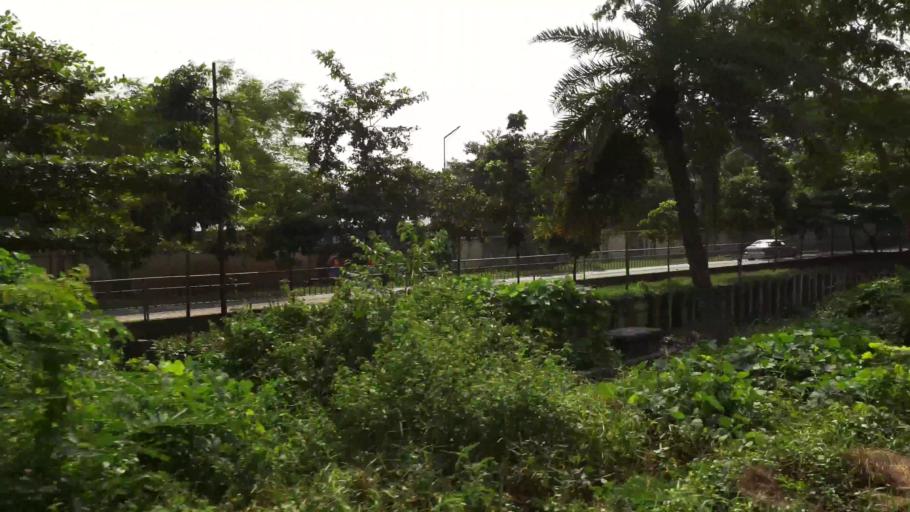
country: BD
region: Dhaka
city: Tungi
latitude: 23.8478
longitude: 90.4119
